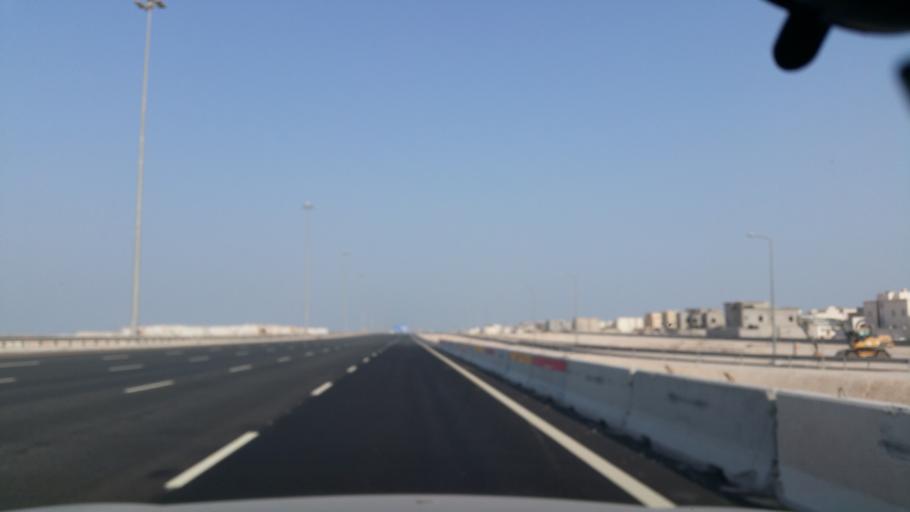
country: QA
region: Baladiyat Umm Salal
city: Umm Salal `Ali
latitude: 25.4567
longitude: 51.4516
